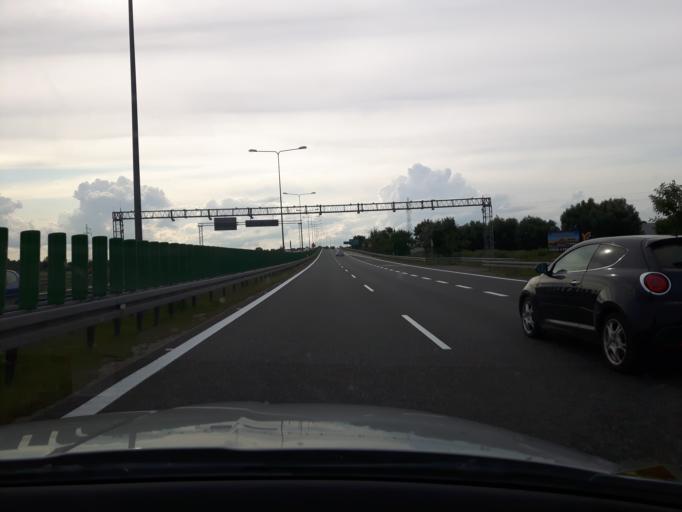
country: PL
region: Warmian-Masurian Voivodeship
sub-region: Powiat elblaski
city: Elblag
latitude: 54.1466
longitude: 19.3811
